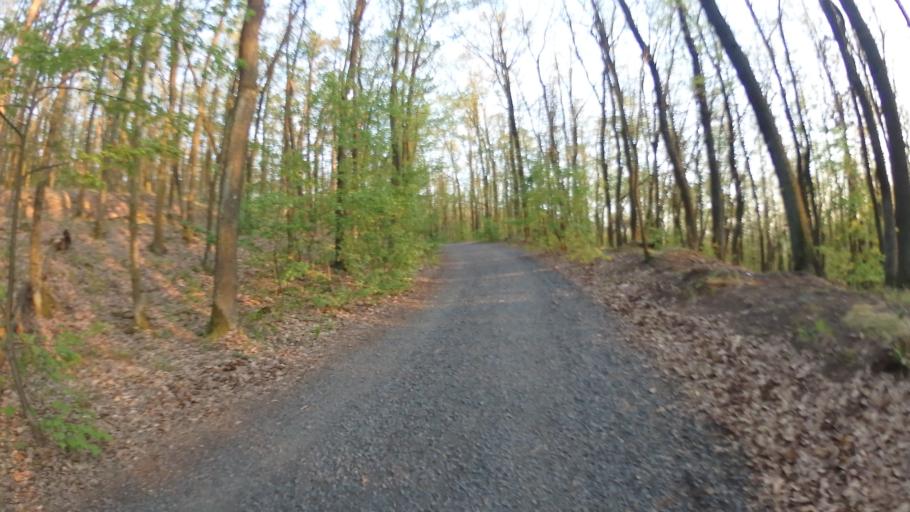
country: CZ
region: South Moravian
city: Troubsko
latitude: 49.1917
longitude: 16.5153
